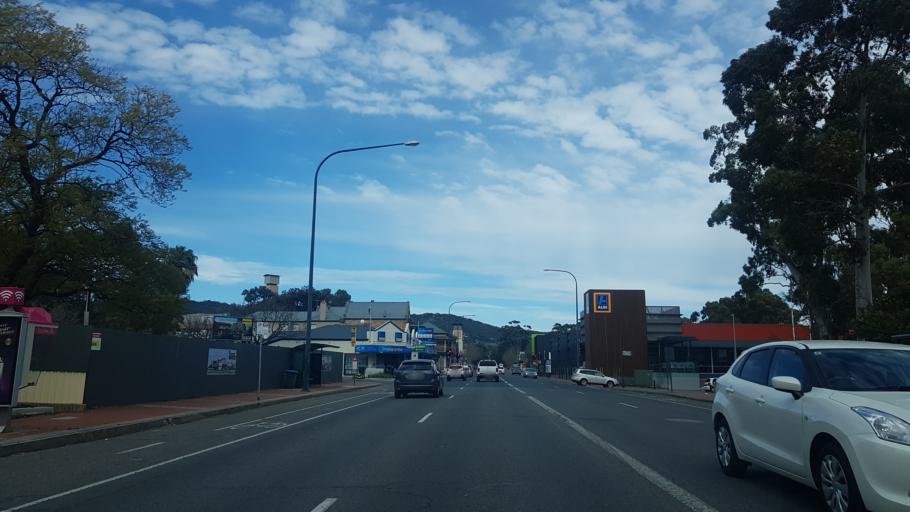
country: AU
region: South Australia
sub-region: Mitcham
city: Hawthorn
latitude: -34.9729
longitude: 138.6092
